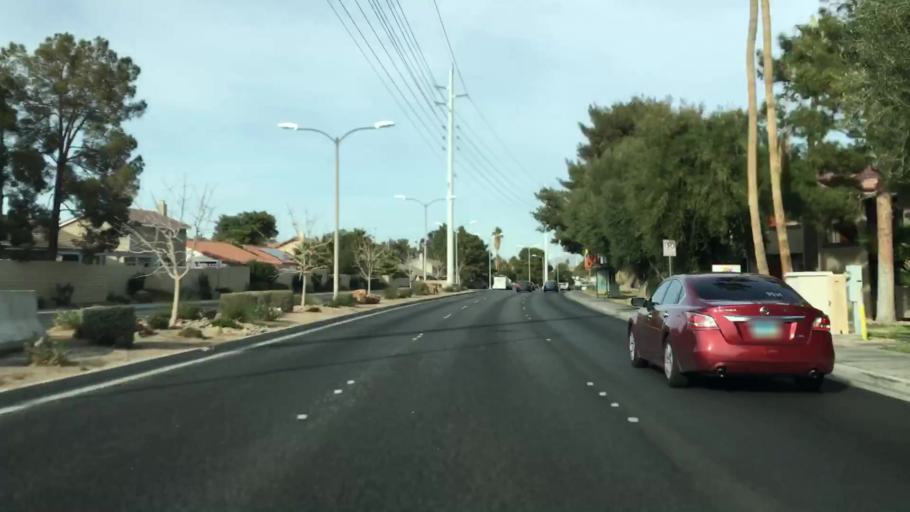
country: US
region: Nevada
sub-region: Clark County
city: Whitney
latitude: 36.0612
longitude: -115.0848
